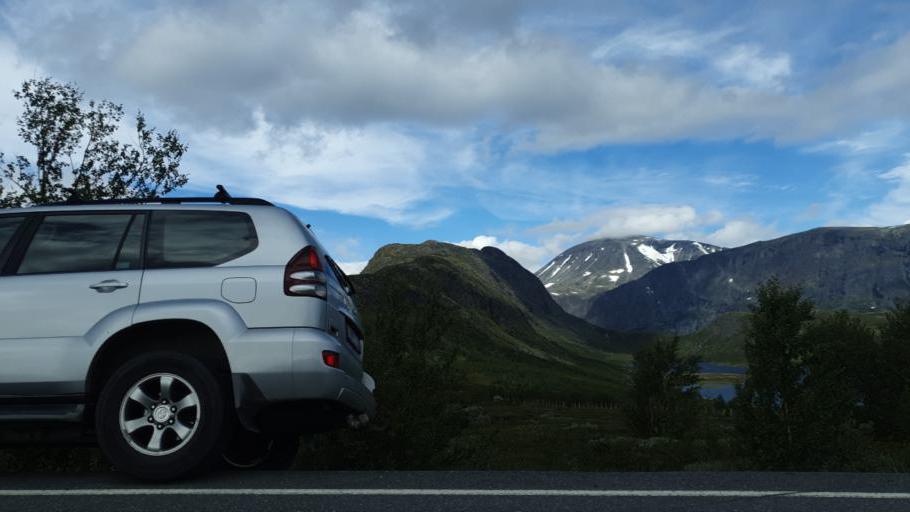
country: NO
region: Oppland
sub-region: Vang
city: Vang
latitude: 61.4637
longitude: 8.8074
